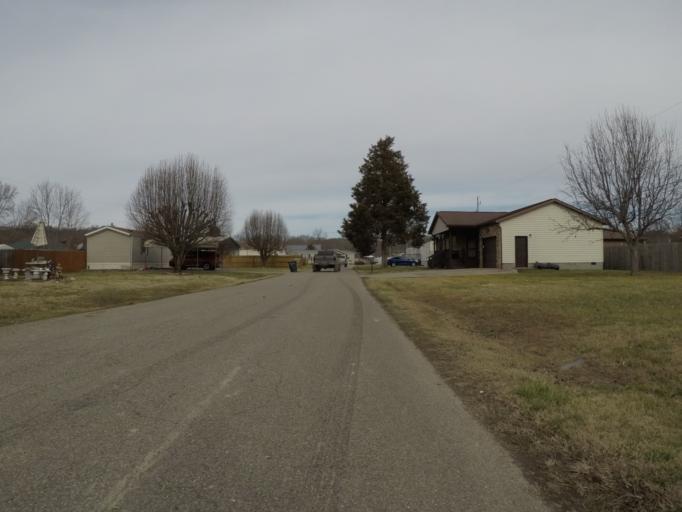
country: US
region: West Virginia
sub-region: Cabell County
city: Pea Ridge
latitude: 38.4523
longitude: -82.3470
